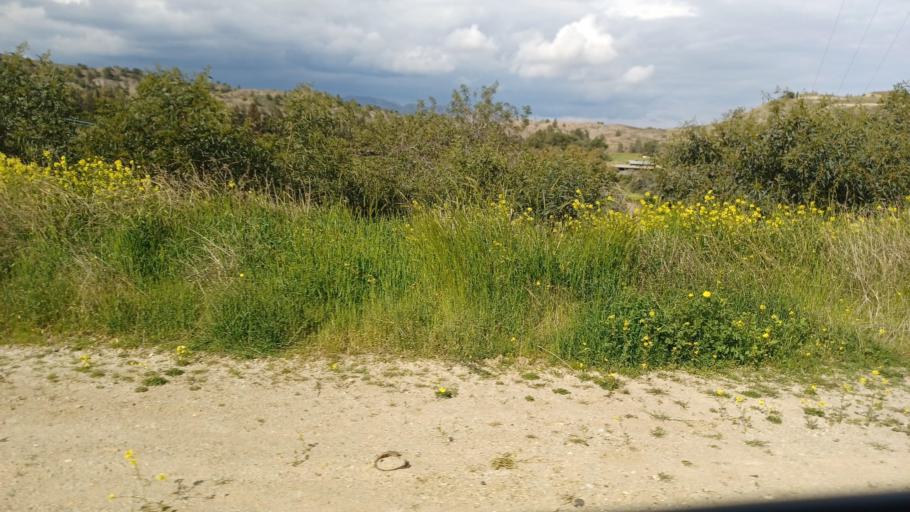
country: CY
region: Lefkosia
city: Lefka
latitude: 35.0947
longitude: 32.8835
